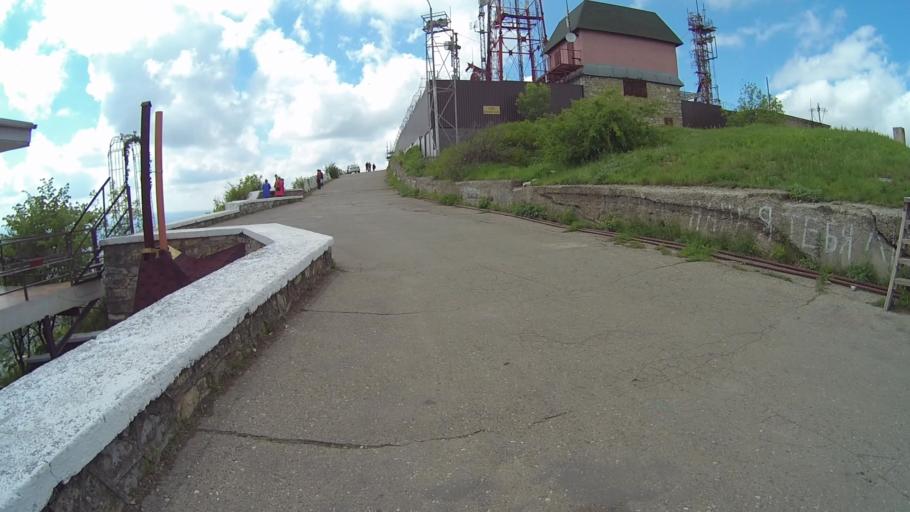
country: RU
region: Stavropol'skiy
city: Goryachevodskiy
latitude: 44.0498
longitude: 43.0889
